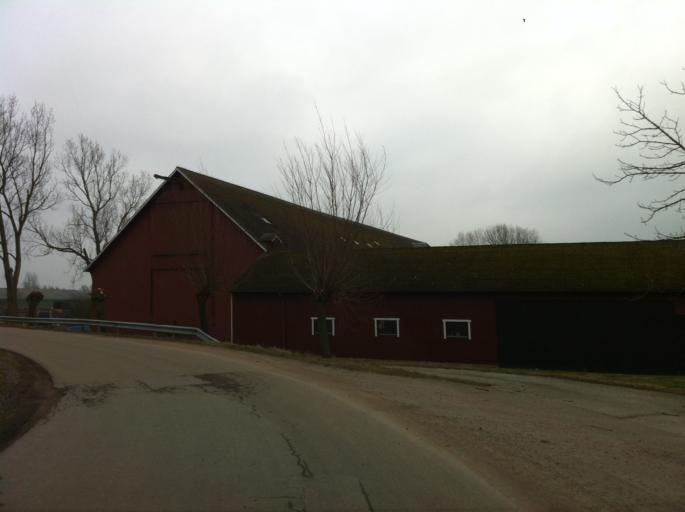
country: SE
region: Skane
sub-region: Landskrona
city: Asmundtorp
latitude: 55.9288
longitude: 13.0024
